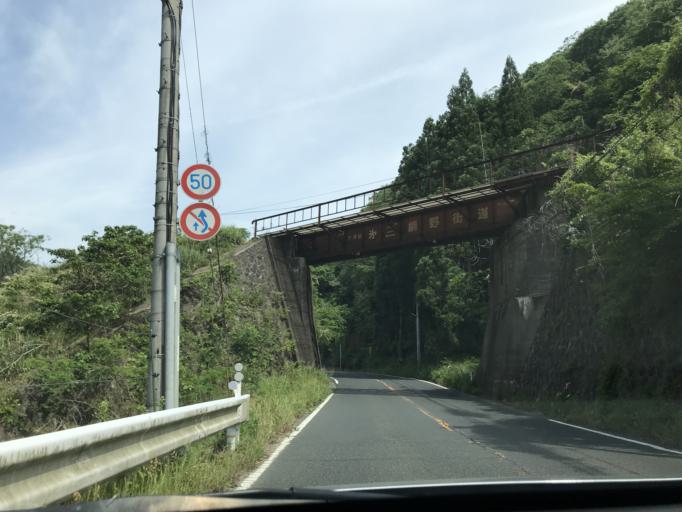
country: JP
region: Kyoto
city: Miyazu
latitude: 35.6618
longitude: 135.0170
